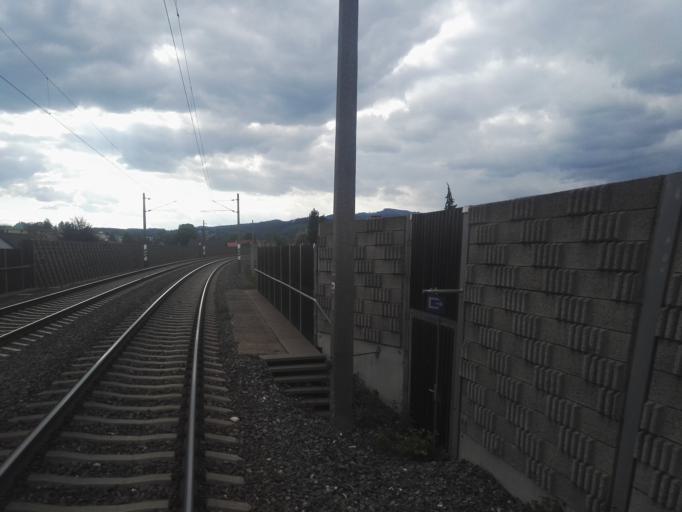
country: AT
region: Styria
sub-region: Politischer Bezirk Graz-Umgebung
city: Gratkorn
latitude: 47.1176
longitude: 15.3490
